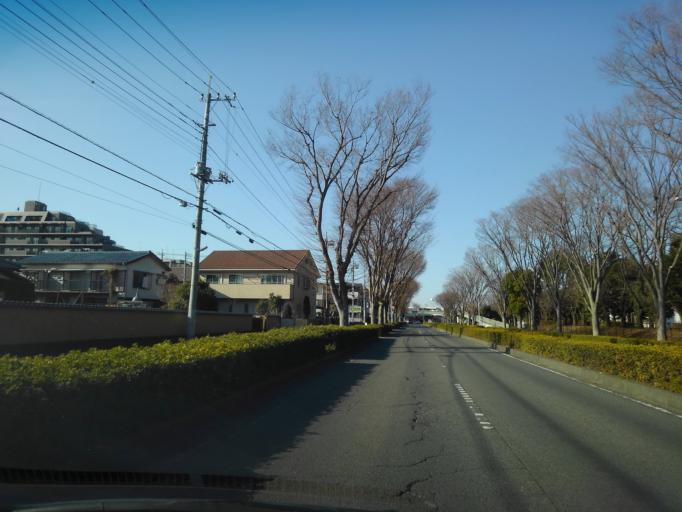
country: JP
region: Saitama
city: Tokorozawa
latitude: 35.8048
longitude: 139.4623
